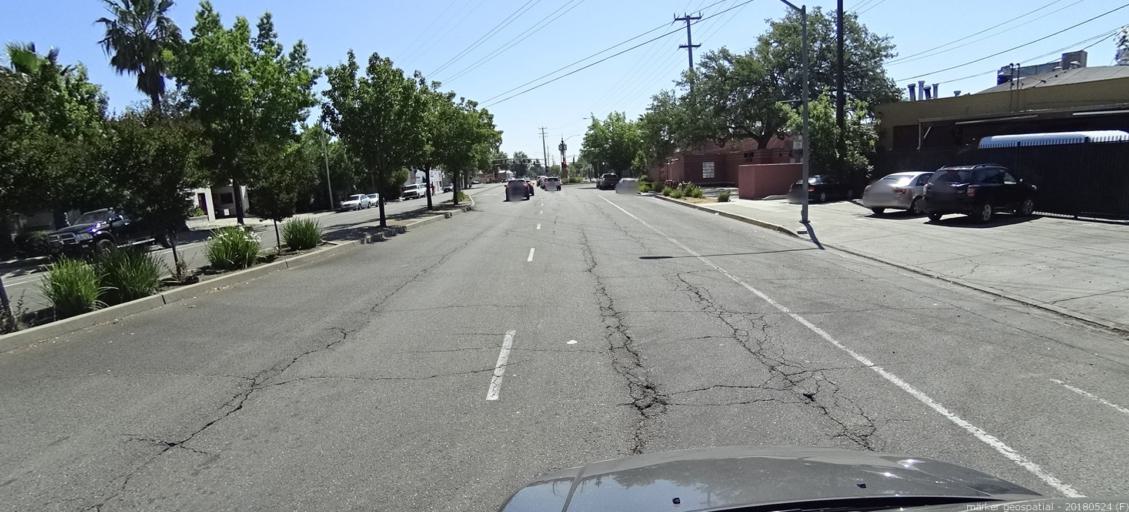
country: US
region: California
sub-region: Sacramento County
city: Sacramento
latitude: 38.6063
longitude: -121.4605
